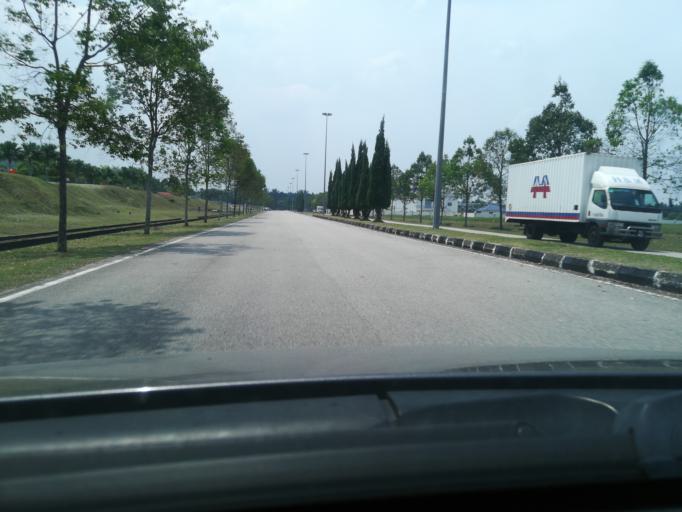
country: MY
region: Kedah
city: Kulim
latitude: 5.4275
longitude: 100.5775
